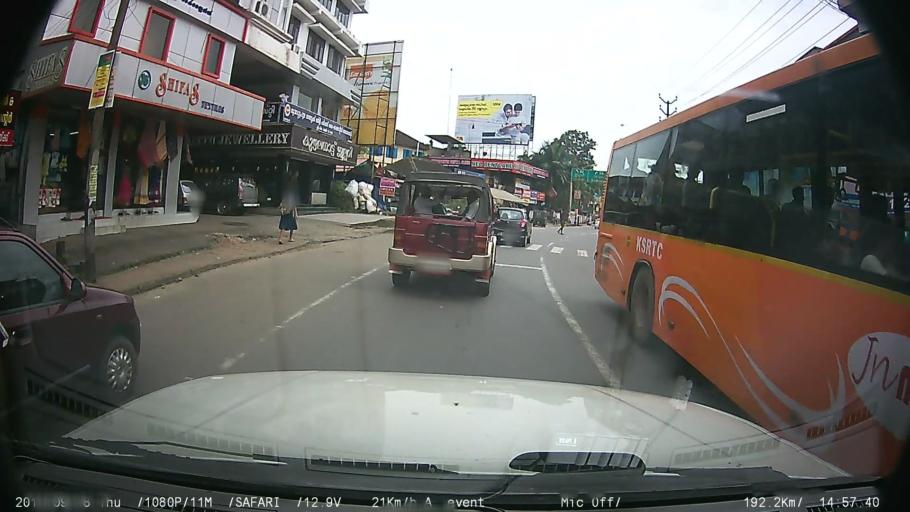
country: IN
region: Kerala
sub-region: Ernakulam
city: Muvattupula
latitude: 9.9816
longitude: 76.5802
